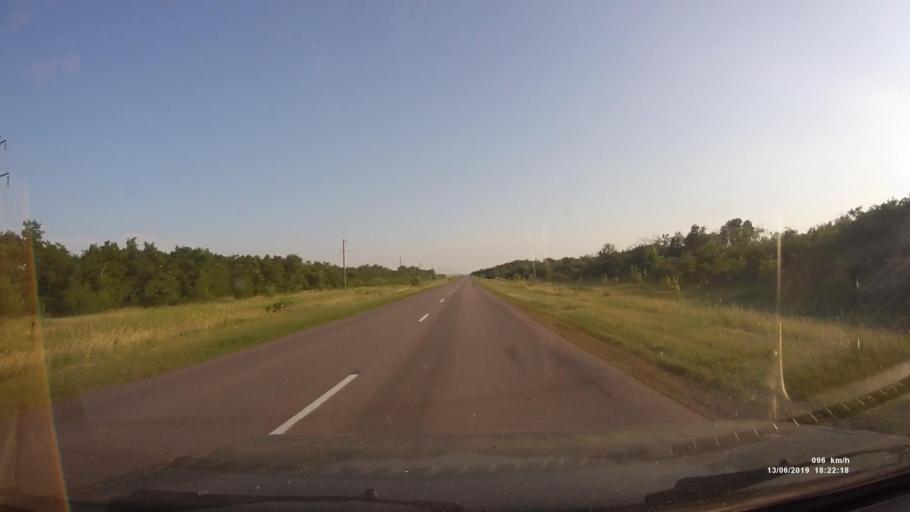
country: RU
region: Rostov
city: Kazanskaya
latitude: 49.8604
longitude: 41.2800
